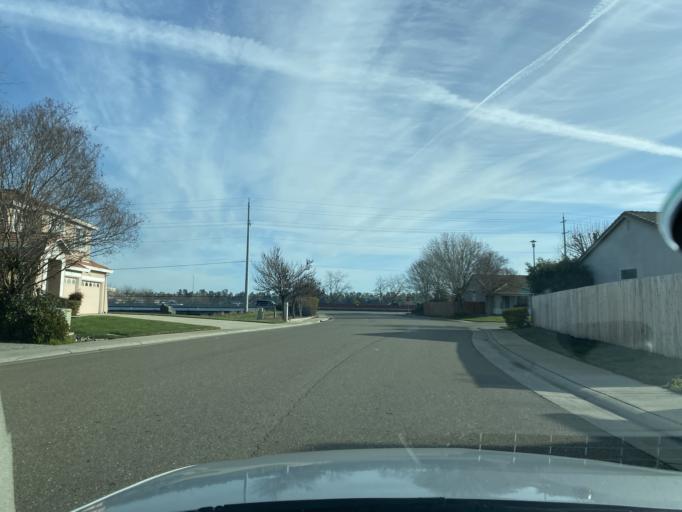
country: US
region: California
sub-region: Sacramento County
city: Laguna
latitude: 38.4299
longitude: -121.3999
